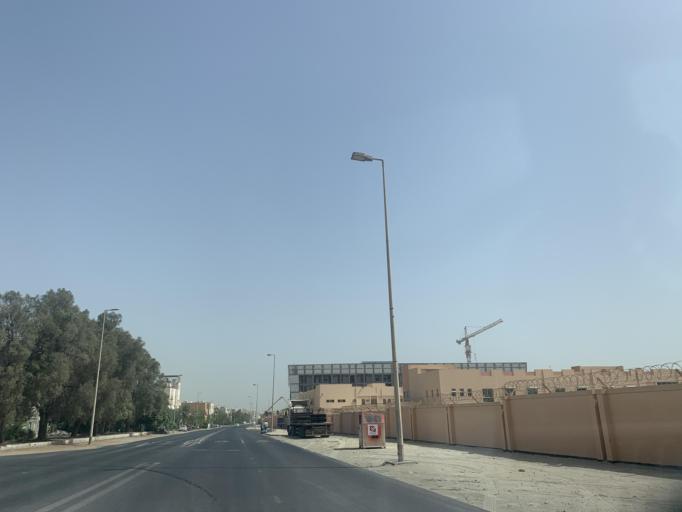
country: BH
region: Northern
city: Madinat `Isa
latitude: 26.1540
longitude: 50.5257
